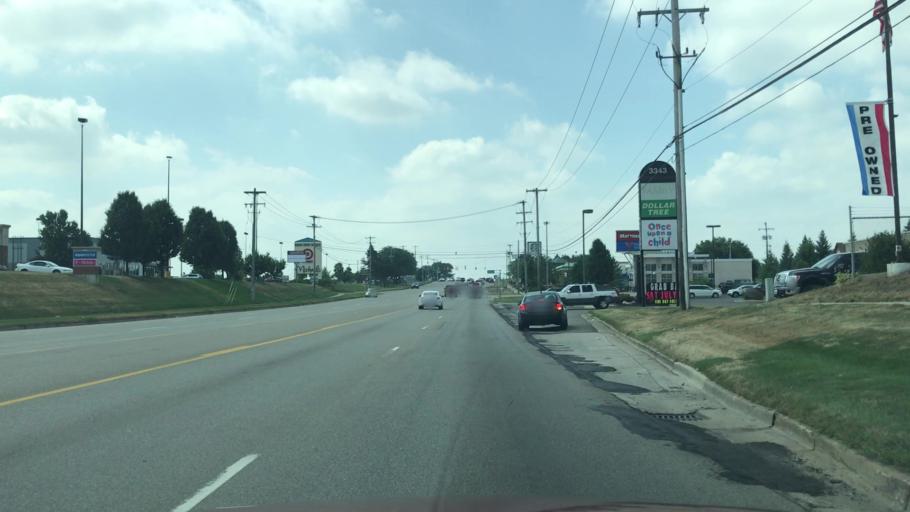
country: US
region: Michigan
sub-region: Kent County
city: Comstock Park
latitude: 43.0244
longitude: -85.6892
